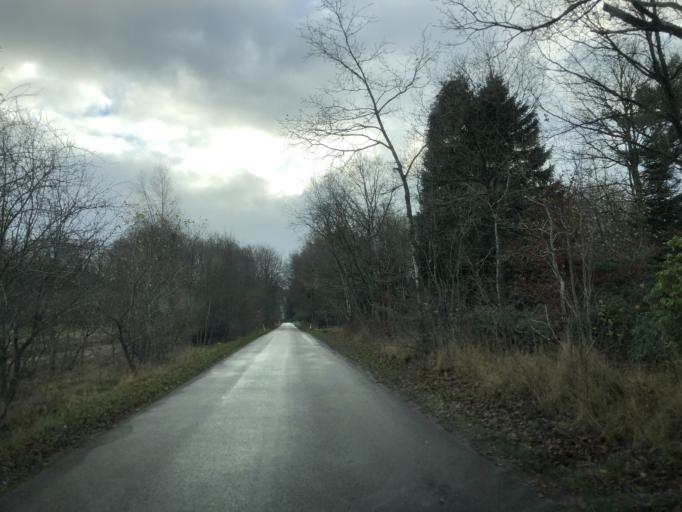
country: DK
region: North Denmark
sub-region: Rebild Kommune
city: Stovring
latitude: 56.9290
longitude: 9.8045
